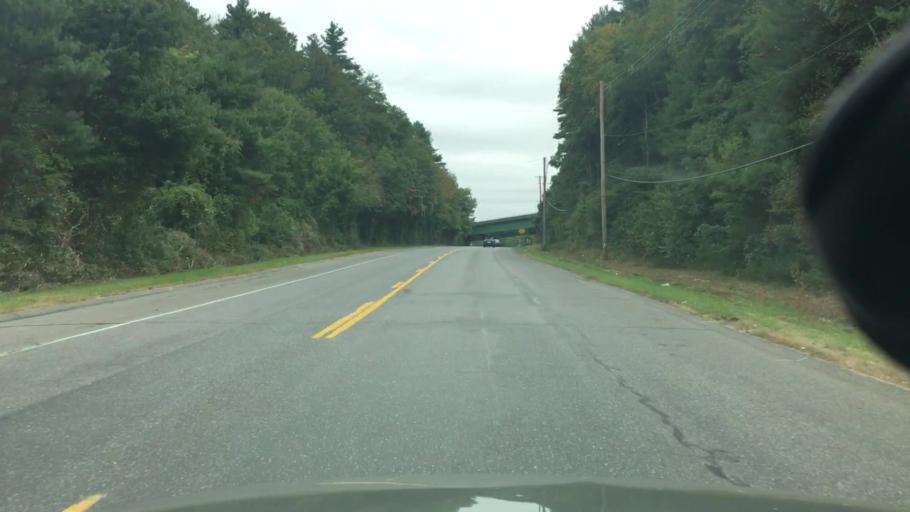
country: US
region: Massachusetts
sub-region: Worcester County
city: Sturbridge
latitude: 42.0683
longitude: -72.1047
